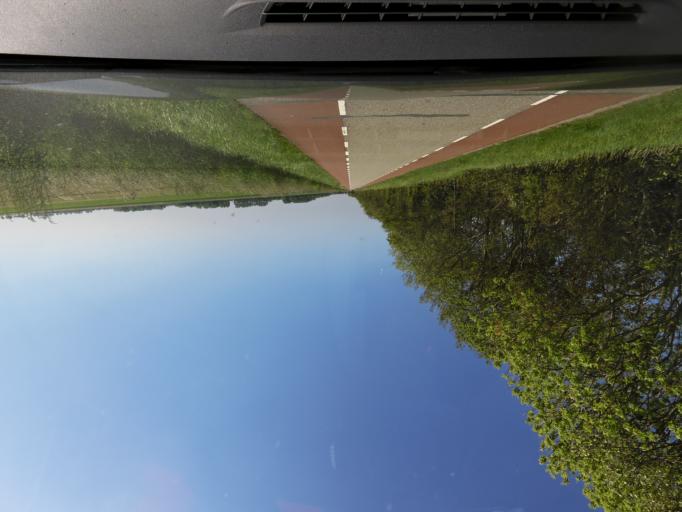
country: NL
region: South Holland
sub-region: Gemeente Goeree-Overflakkee
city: Dirksland
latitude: 51.7858
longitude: 4.0430
